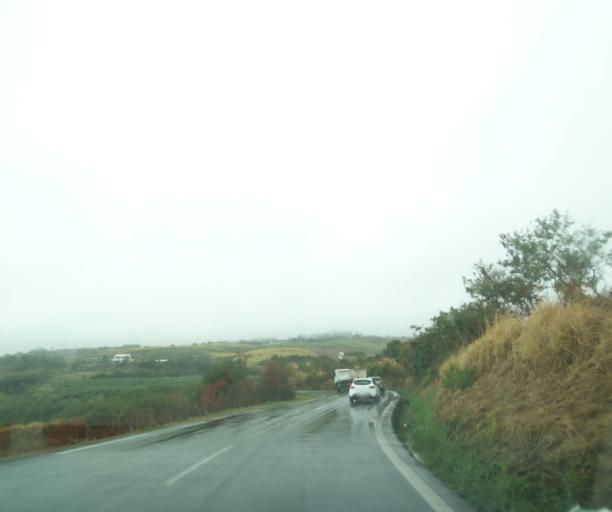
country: RE
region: Reunion
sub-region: Reunion
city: Saint-Paul
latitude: -21.0335
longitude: 55.2780
